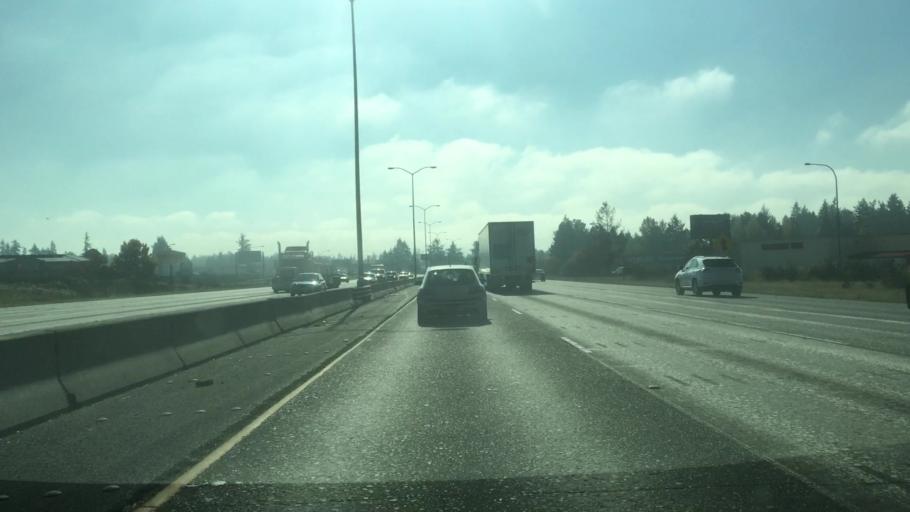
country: US
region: Washington
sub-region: Pierce County
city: Parkland
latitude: 47.1805
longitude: -122.4652
